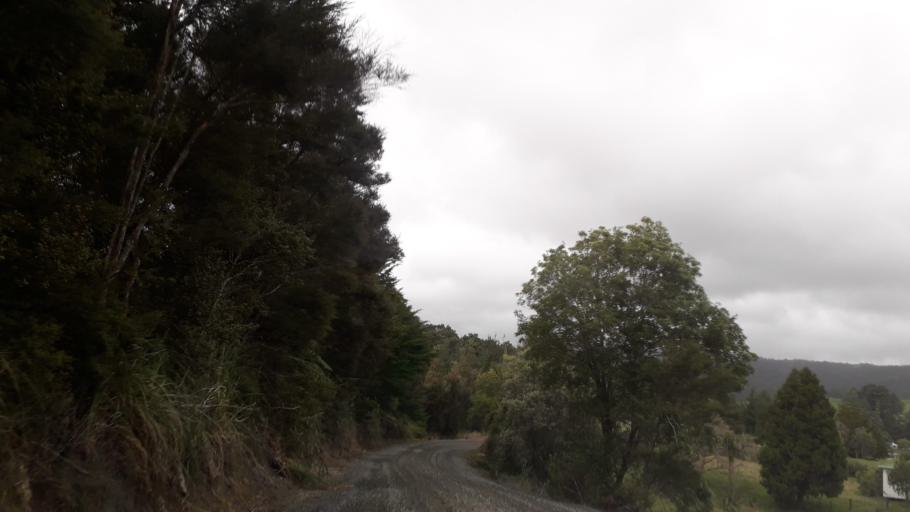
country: NZ
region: Northland
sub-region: Far North District
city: Waimate North
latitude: -35.1454
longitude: 173.7129
